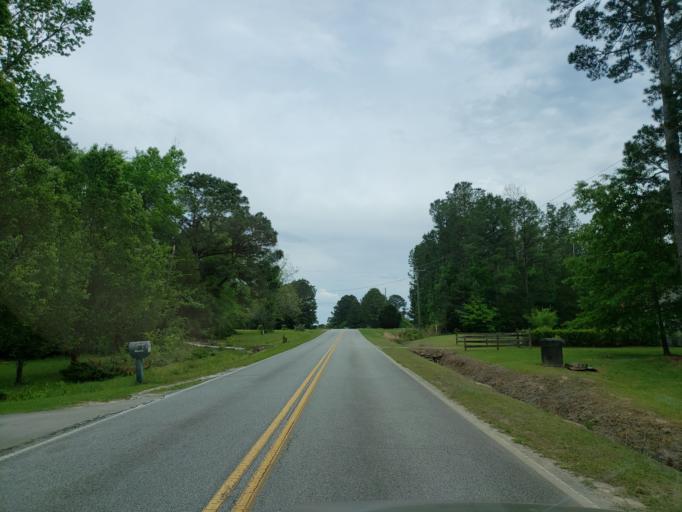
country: US
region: Georgia
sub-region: Bibb County
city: West Point
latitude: 32.8222
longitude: -83.8693
